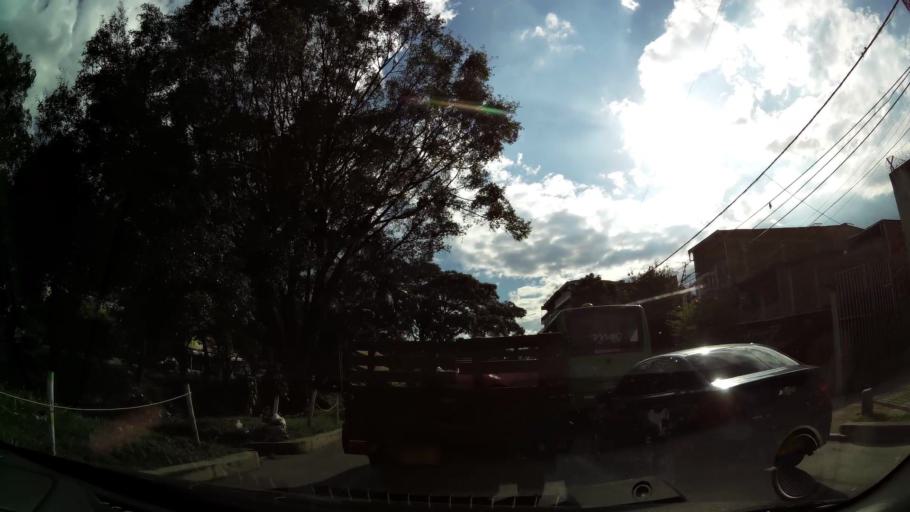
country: CO
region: Valle del Cauca
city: Cali
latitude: 3.4026
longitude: -76.5103
